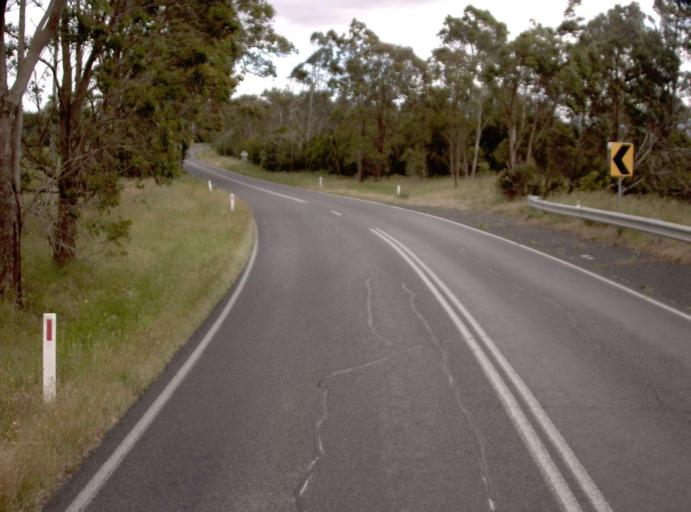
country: AU
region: Victoria
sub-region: Latrobe
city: Moe
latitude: -38.1295
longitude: 146.2569
